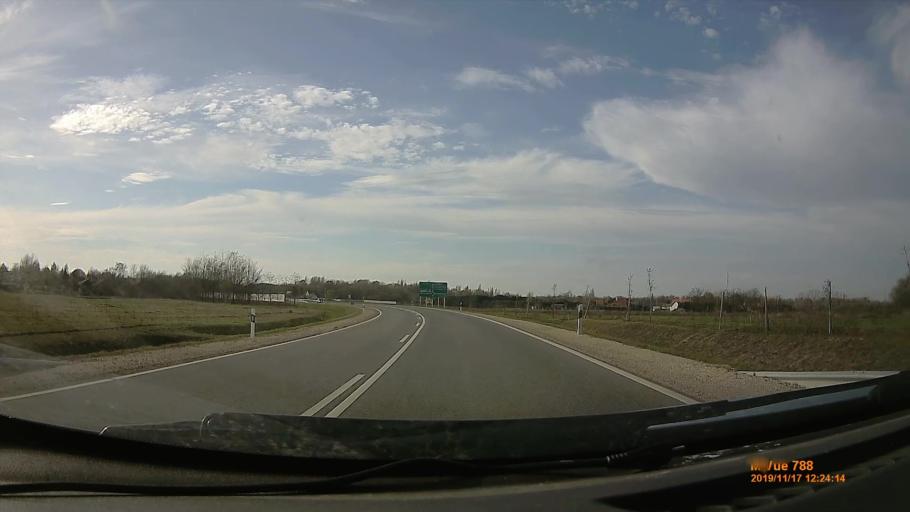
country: HU
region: Bacs-Kiskun
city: Kecskemet
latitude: 46.9379
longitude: 19.6446
